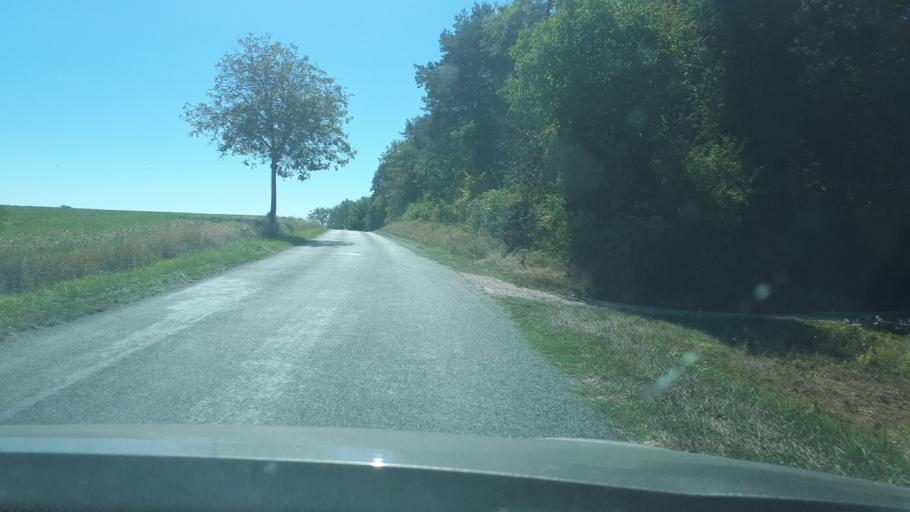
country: FR
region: Centre
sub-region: Departement du Cher
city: Sancerre
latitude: 47.2742
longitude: 2.7674
